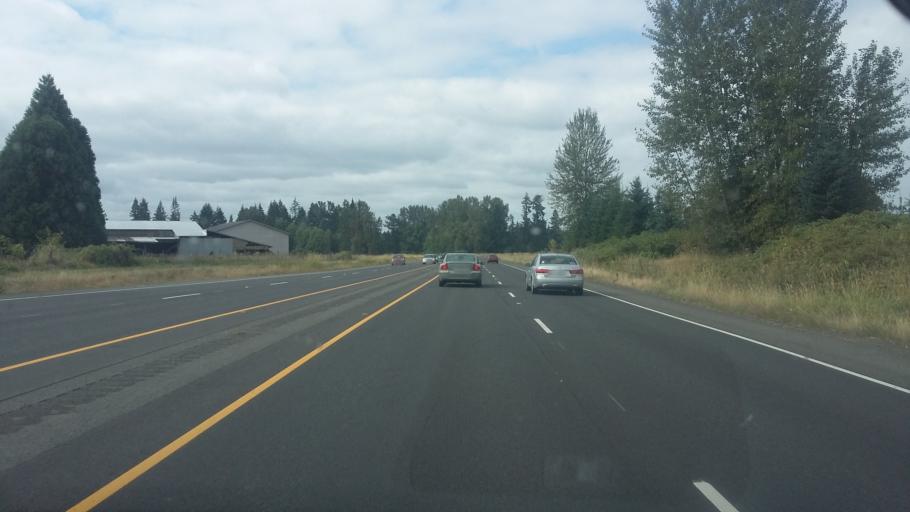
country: US
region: Washington
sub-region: Clark County
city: Meadow Glade
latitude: 45.7503
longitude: -122.5486
